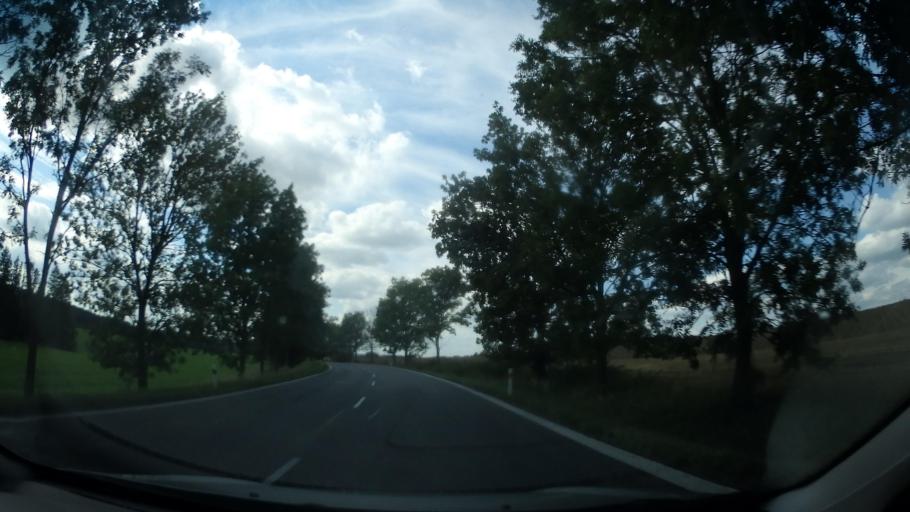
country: CZ
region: Vysocina
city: Pribyslav
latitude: 49.5645
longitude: 15.7977
